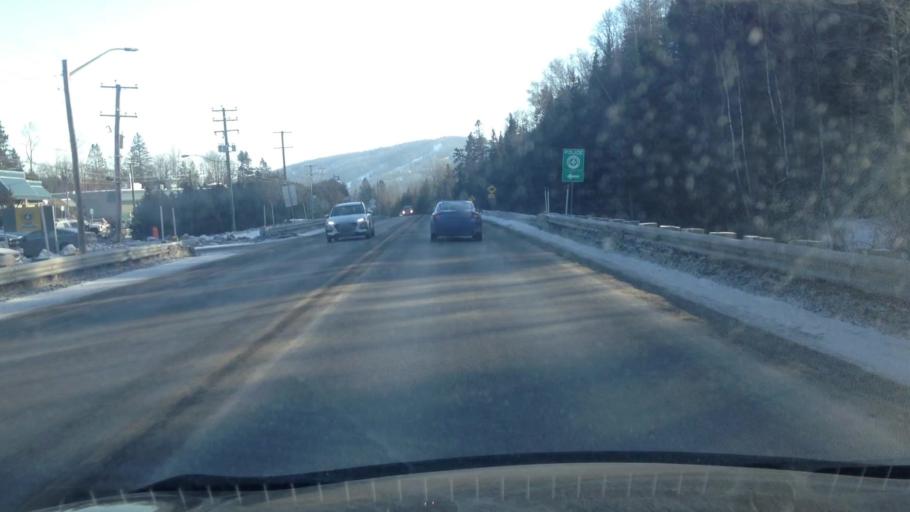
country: CA
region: Quebec
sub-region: Laurentides
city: Saint-Sauveur
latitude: 45.8859
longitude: -74.1833
